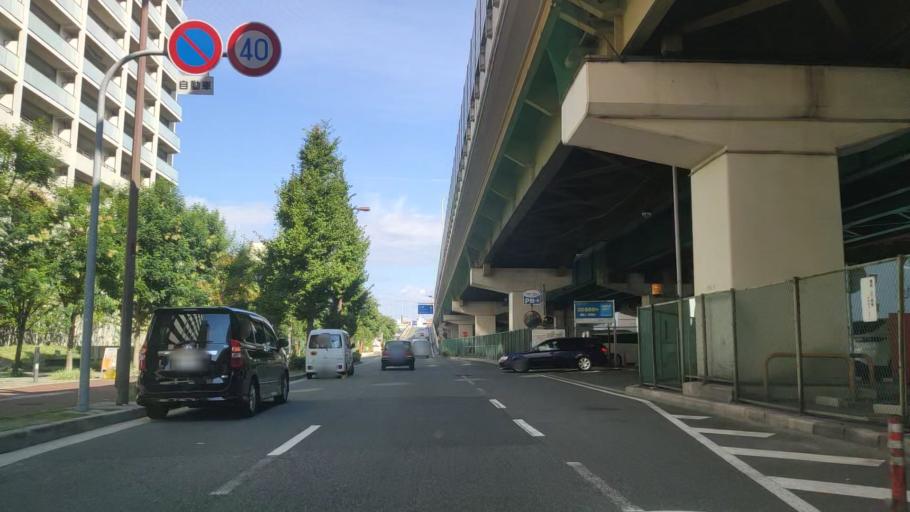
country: JP
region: Osaka
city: Suita
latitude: 34.7459
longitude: 135.4976
